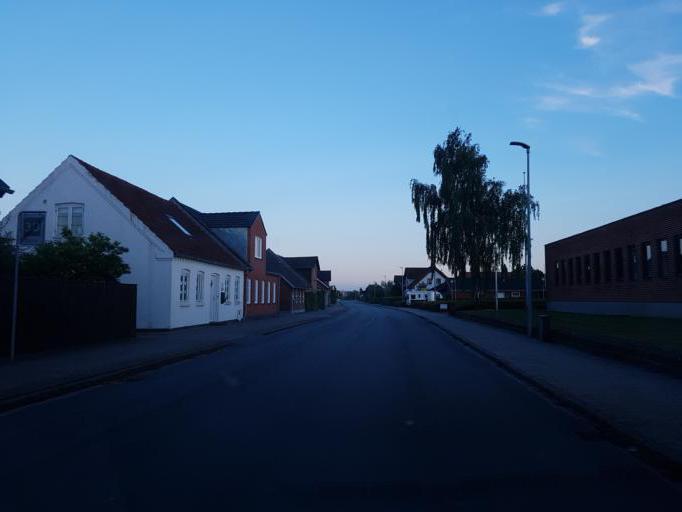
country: DK
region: South Denmark
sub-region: Vejen Kommune
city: Vejen
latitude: 55.4710
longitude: 9.1359
